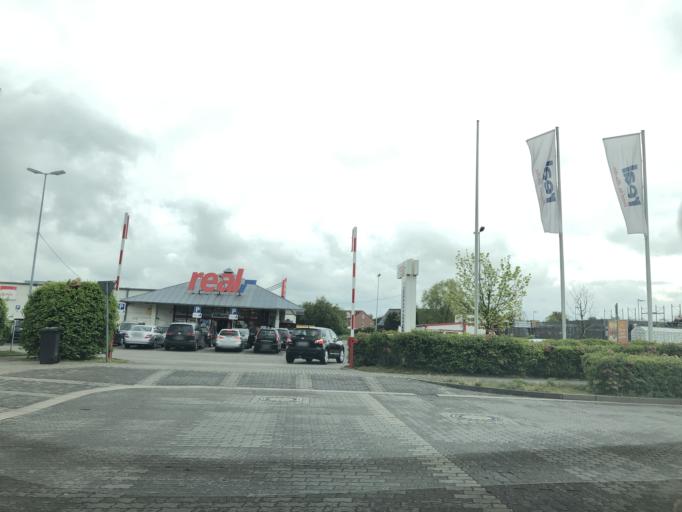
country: DE
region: Brandenburg
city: Pritzwalk
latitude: 53.1584
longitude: 12.1729
